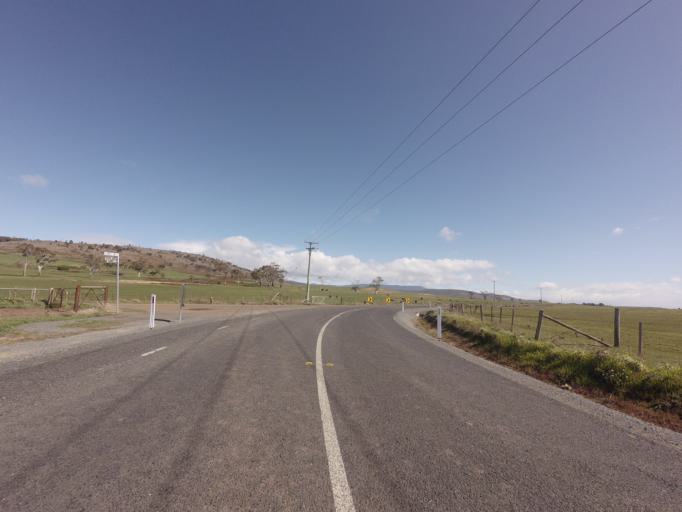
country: AU
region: Tasmania
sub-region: Northern Midlands
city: Evandale
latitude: -41.9122
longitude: 147.3776
